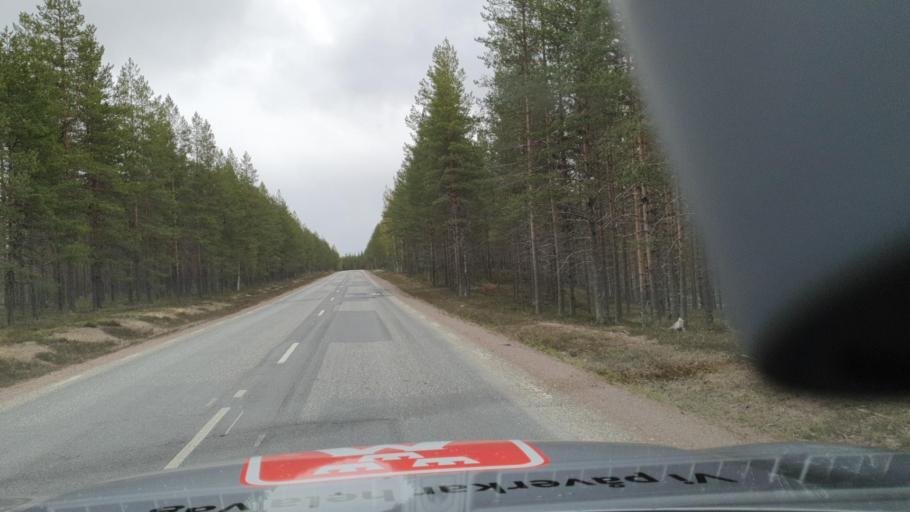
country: SE
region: Vaesternorrland
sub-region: Solleftea Kommun
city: Solleftea
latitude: 63.6448
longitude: 17.3936
